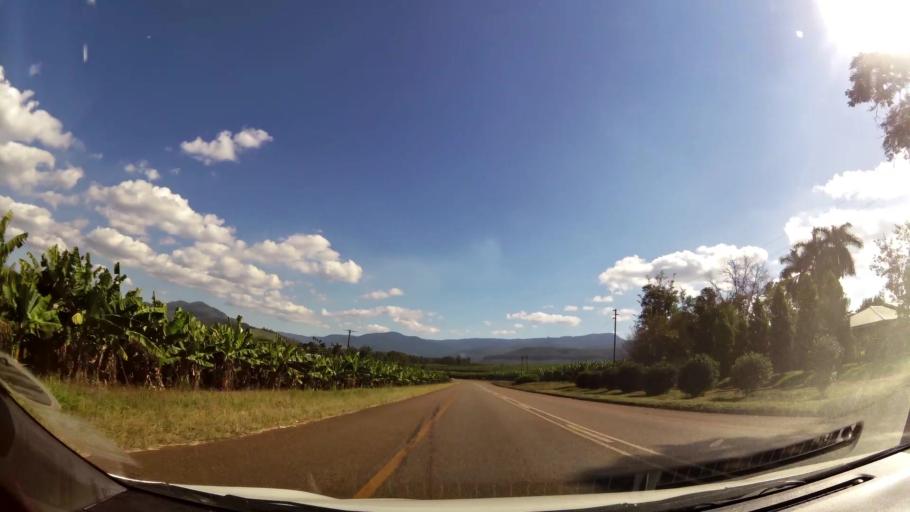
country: ZA
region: Limpopo
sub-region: Mopani District Municipality
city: Tzaneen
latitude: -23.8030
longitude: 30.1187
